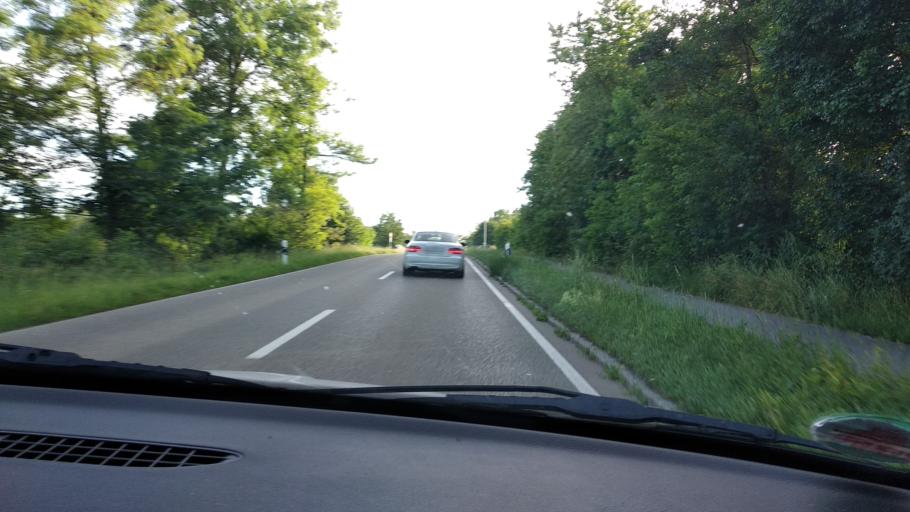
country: DE
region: Bavaria
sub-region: Swabia
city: Altenstadt
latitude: 48.1590
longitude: 10.1049
